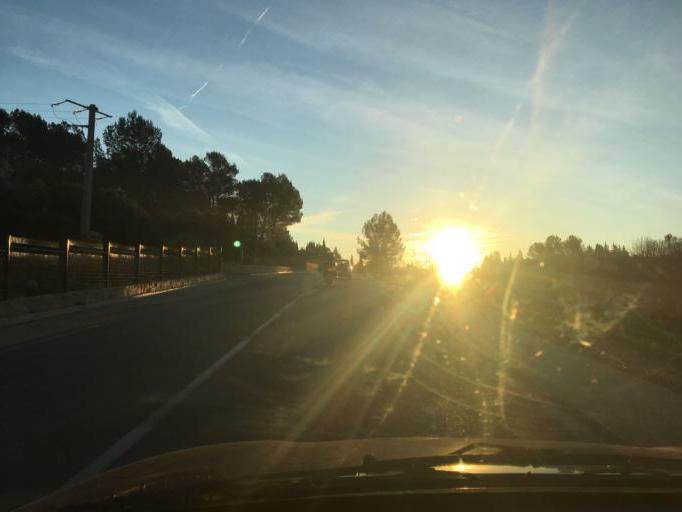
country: FR
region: Provence-Alpes-Cote d'Azur
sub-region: Departement du Var
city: Taradeau
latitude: 43.4662
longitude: 6.3917
